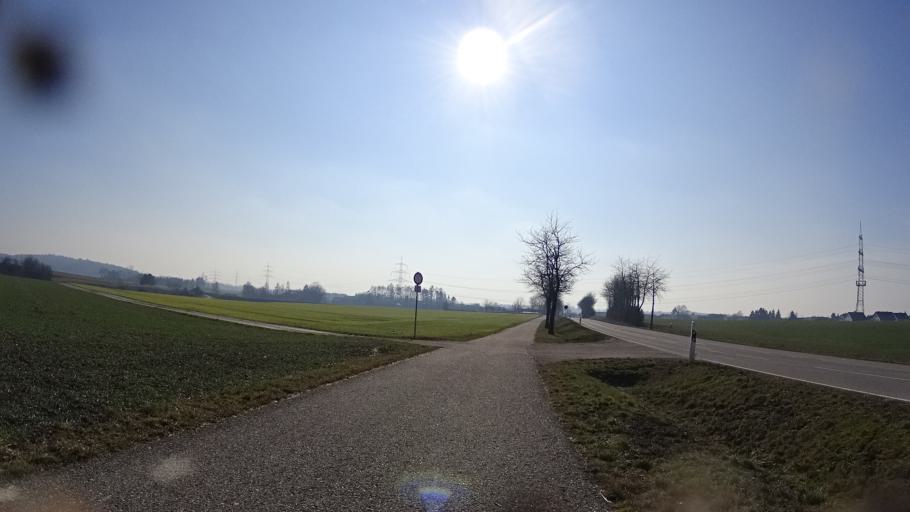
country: DE
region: Bavaria
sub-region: Upper Bavaria
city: Wettstetten
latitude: 48.8342
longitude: 11.4159
